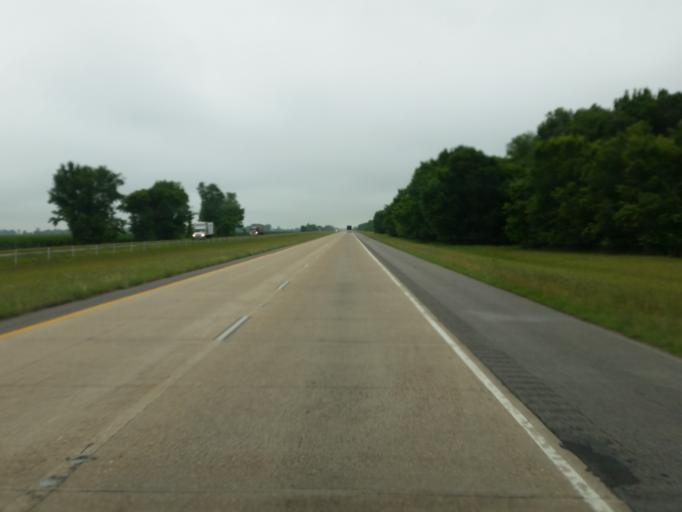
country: US
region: Louisiana
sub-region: Madison Parish
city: Tallulah
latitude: 32.3343
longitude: -91.0521
